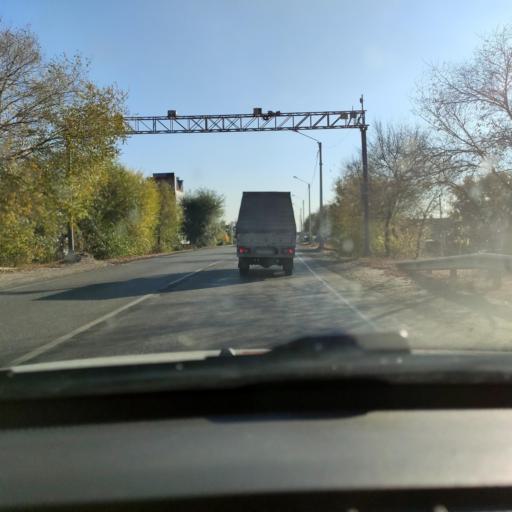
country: RU
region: Voronezj
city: Pridonskoy
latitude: 51.7137
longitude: 39.0747
